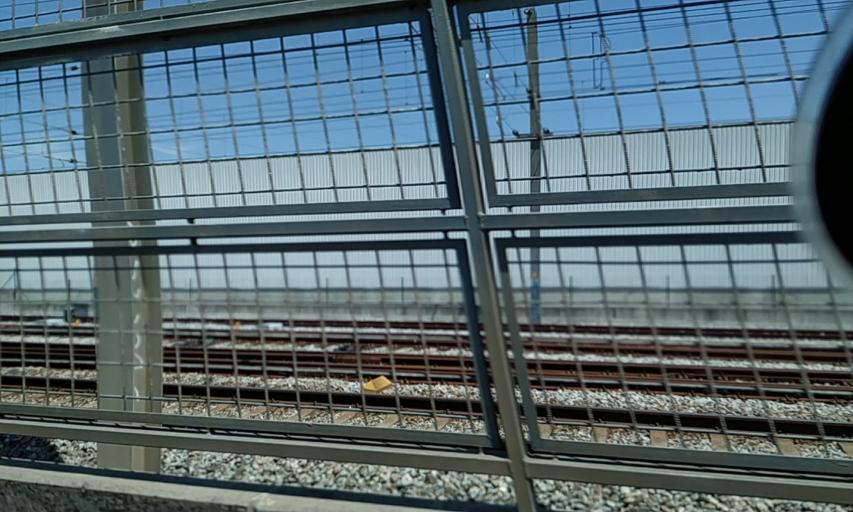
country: PT
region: Setubal
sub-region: Palmela
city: Palmela
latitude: 38.5749
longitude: -8.8737
